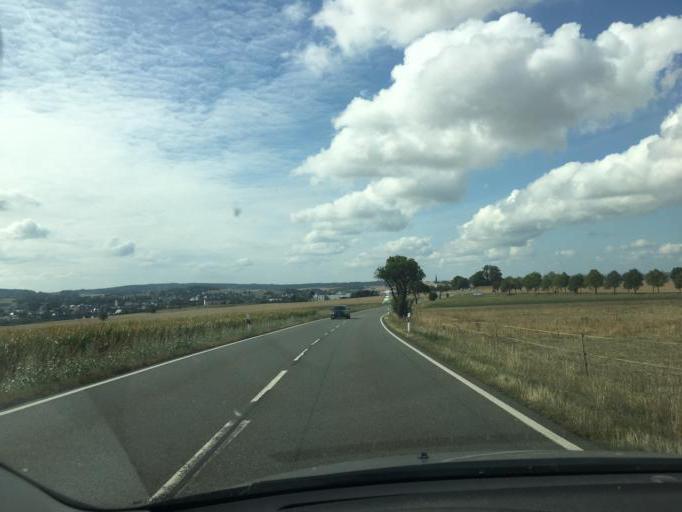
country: DE
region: Thuringia
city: Oettersdorf
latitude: 50.5953
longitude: 11.8210
